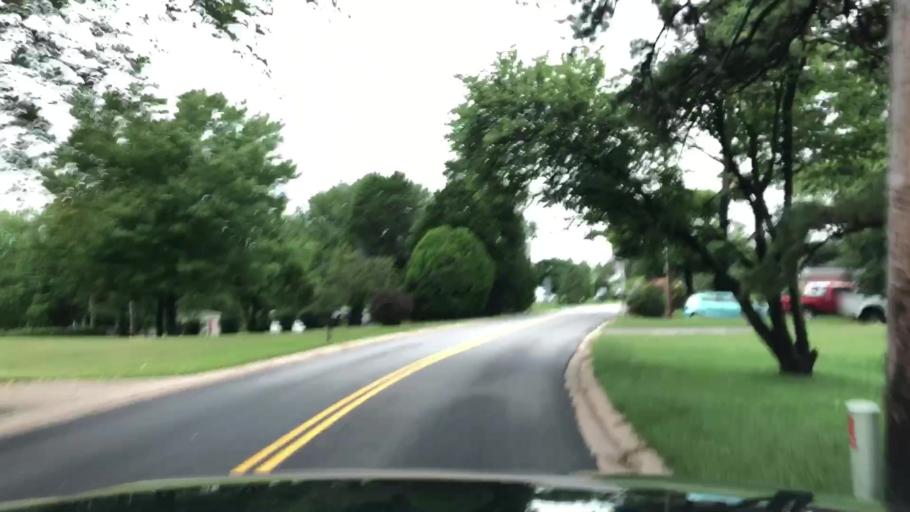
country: US
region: Missouri
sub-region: Saint Louis County
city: Manchester
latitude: 38.5856
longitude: -90.5099
